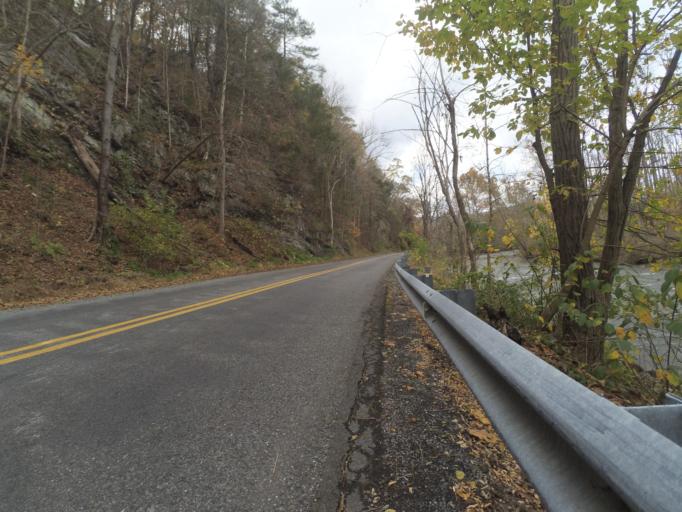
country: US
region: Pennsylvania
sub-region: Centre County
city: Bellefonte
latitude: 40.8940
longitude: -77.7950
